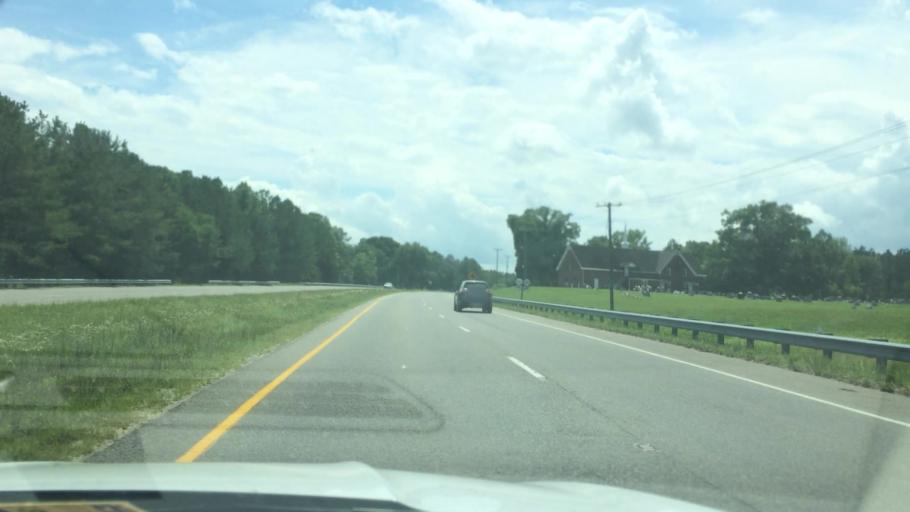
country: US
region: Virginia
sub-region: Middlesex County
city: Saluda
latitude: 37.5601
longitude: -76.6592
